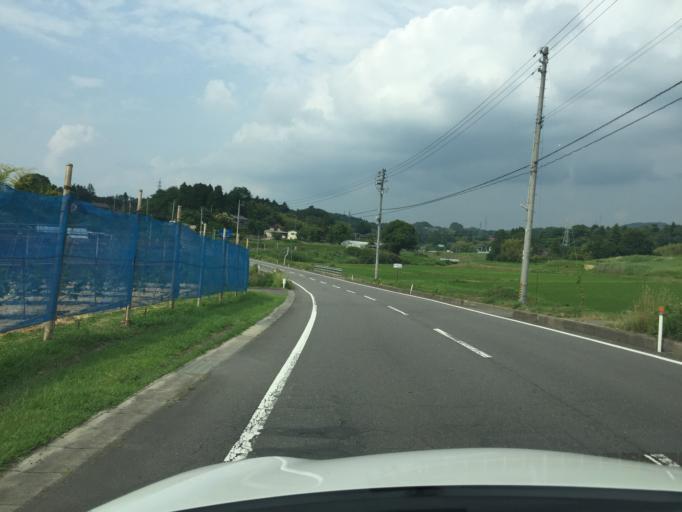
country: JP
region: Fukushima
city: Sukagawa
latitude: 37.2854
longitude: 140.4261
